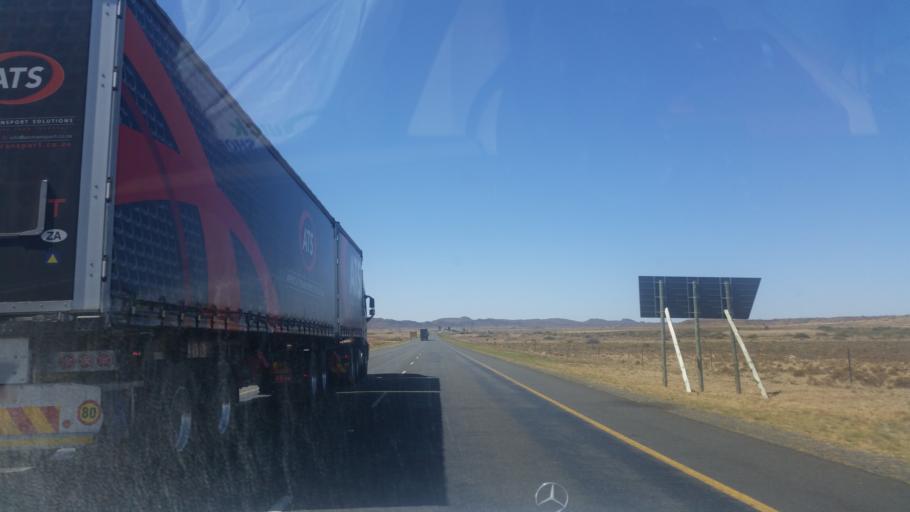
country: ZA
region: Northern Cape
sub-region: Pixley ka Seme District Municipality
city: Colesberg
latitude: -30.6979
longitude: 25.1312
